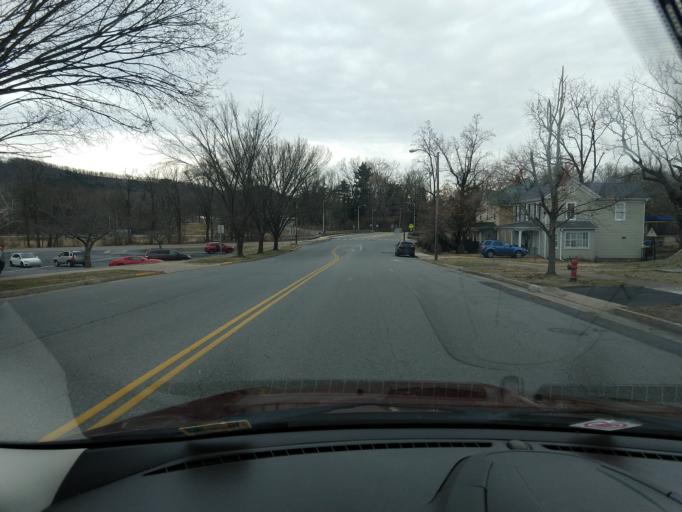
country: US
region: Virginia
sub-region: City of Waynesboro
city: Waynesboro
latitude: 38.0598
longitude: -78.8955
